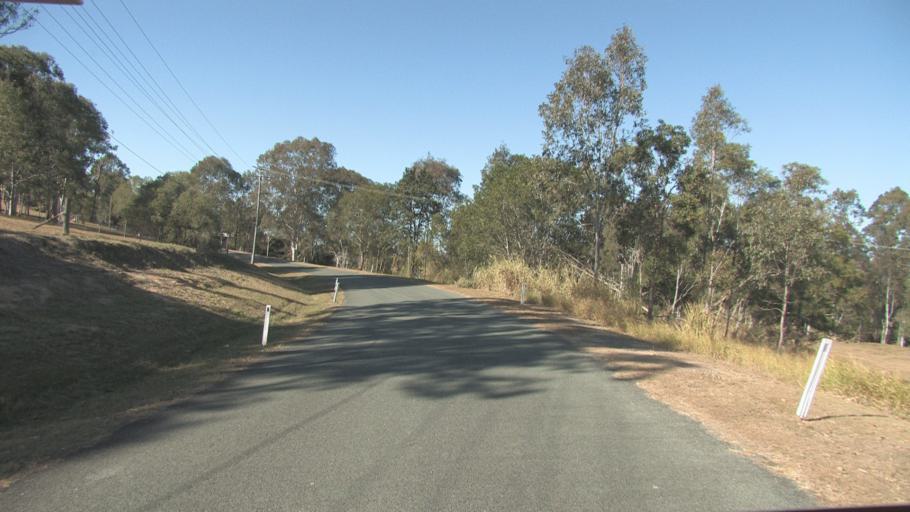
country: AU
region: Queensland
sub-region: Logan
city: North Maclean
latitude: -27.7892
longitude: 153.0065
